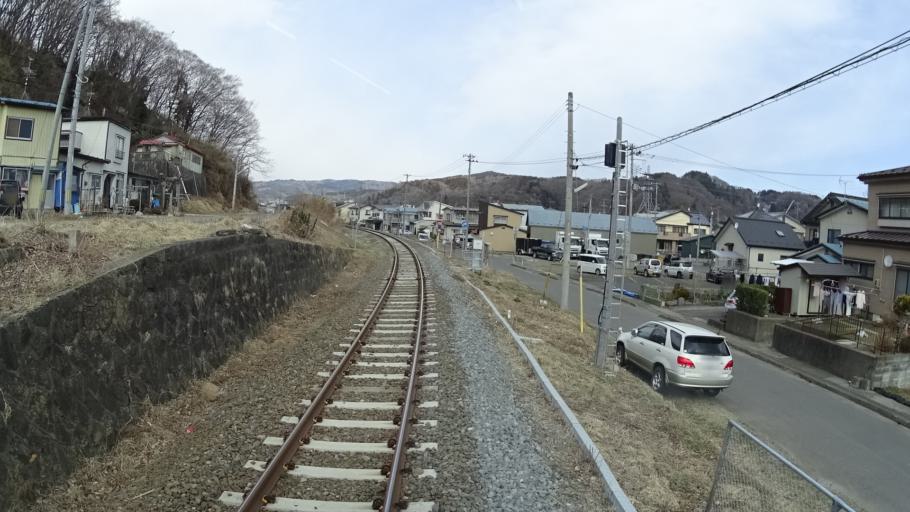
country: JP
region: Iwate
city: Miyako
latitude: 39.6359
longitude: 141.9607
